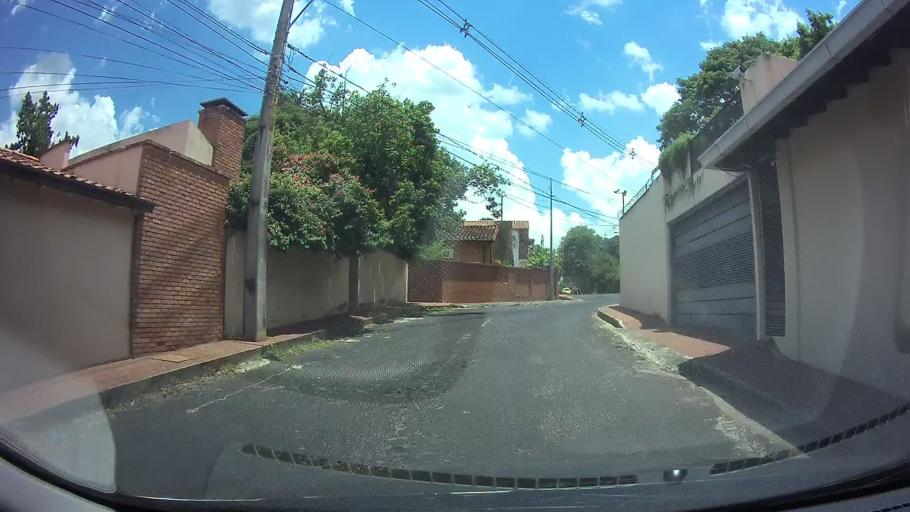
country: PY
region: Asuncion
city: Asuncion
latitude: -25.2982
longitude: -57.5992
